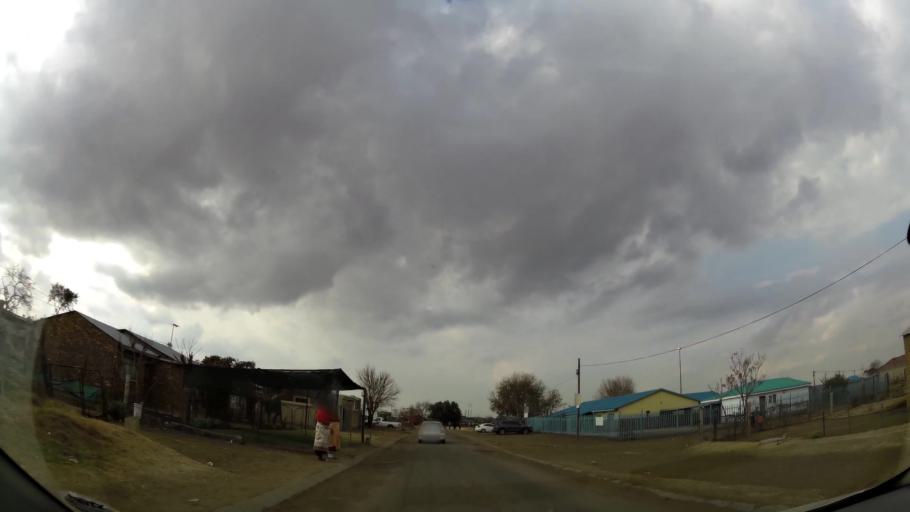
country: ZA
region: Orange Free State
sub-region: Fezile Dabi District Municipality
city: Sasolburg
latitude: -26.8455
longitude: 27.8641
